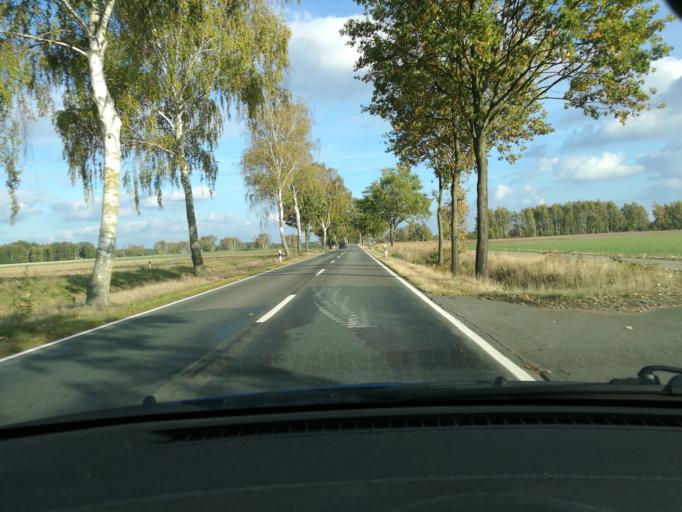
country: DE
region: Lower Saxony
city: Prezelle
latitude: 52.9067
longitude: 11.4029
